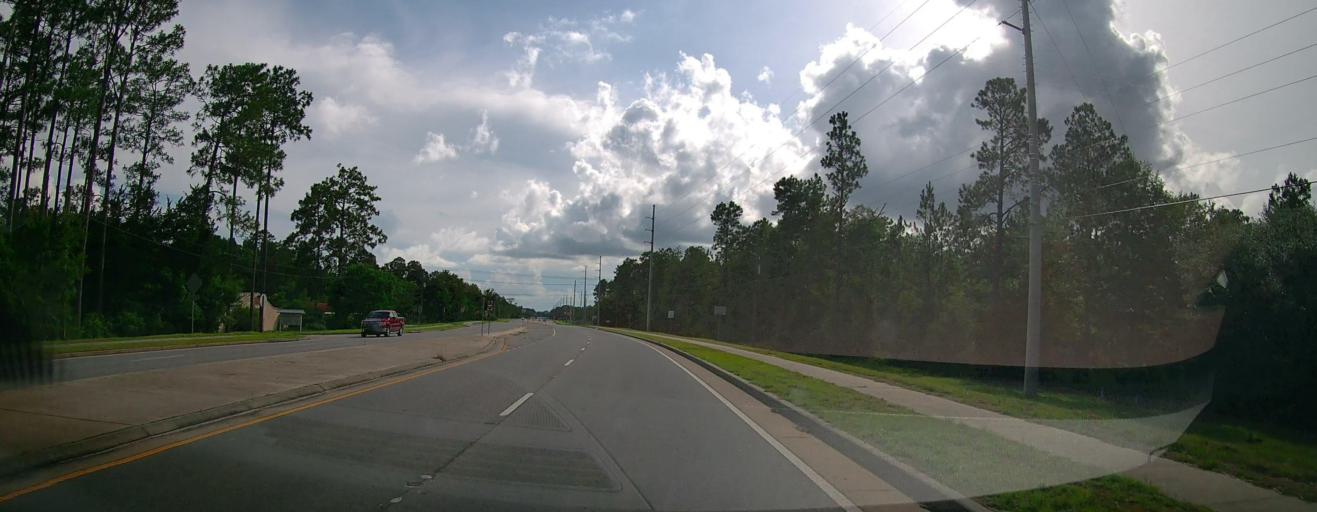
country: US
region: Georgia
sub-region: Wayne County
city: Jesup
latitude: 31.6049
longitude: -81.9198
